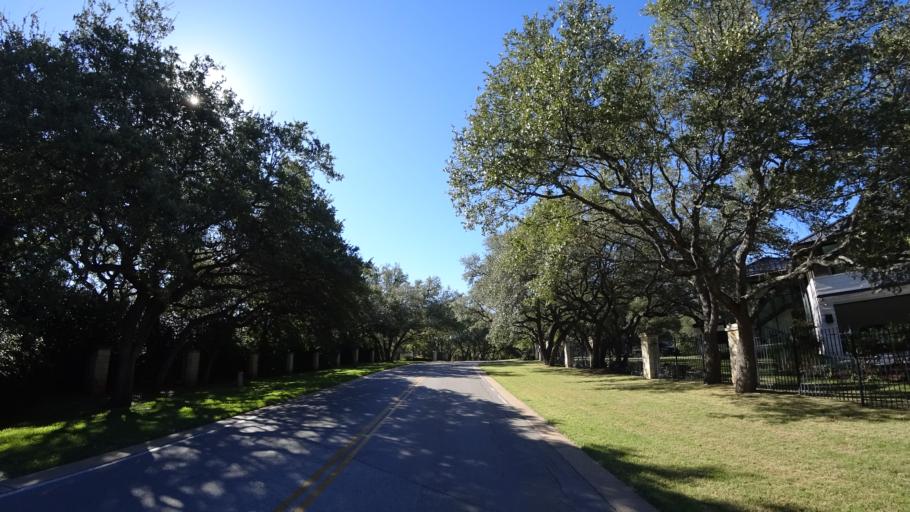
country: US
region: Texas
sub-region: Travis County
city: West Lake Hills
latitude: 30.3388
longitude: -97.7916
